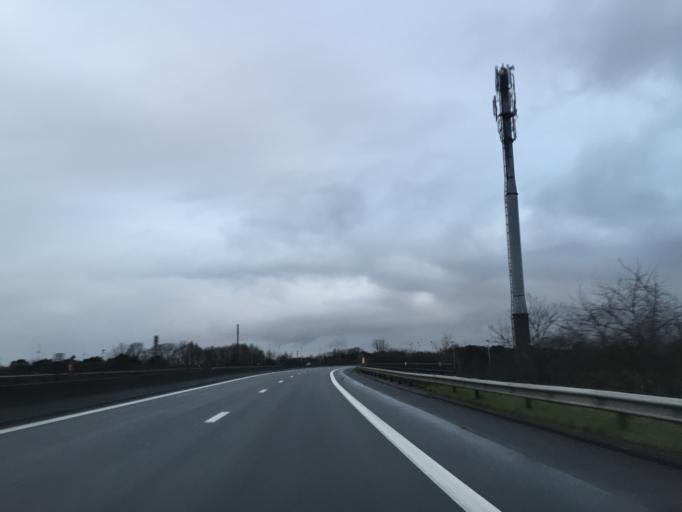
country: BE
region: Flanders
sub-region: Provincie Antwerpen
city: Stabroek
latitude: 51.3546
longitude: 4.3373
